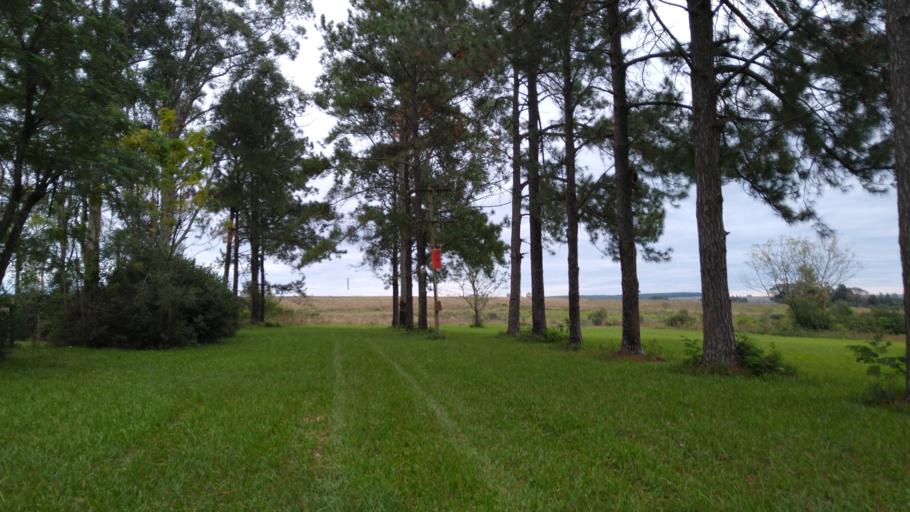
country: PY
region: Itapua
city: San Juan del Parana
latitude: -27.4550
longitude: -56.0562
